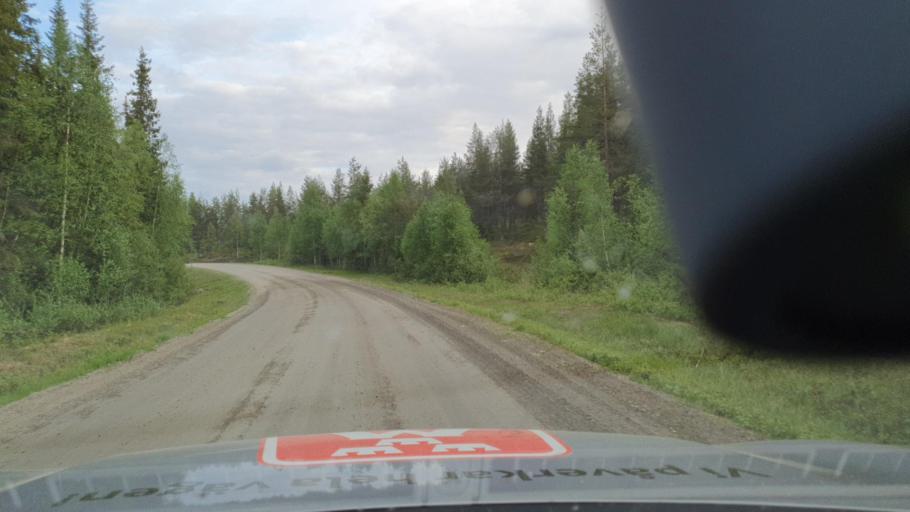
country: SE
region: Norrbotten
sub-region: Gallivare Kommun
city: Gaellivare
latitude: 66.7293
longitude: 21.1428
